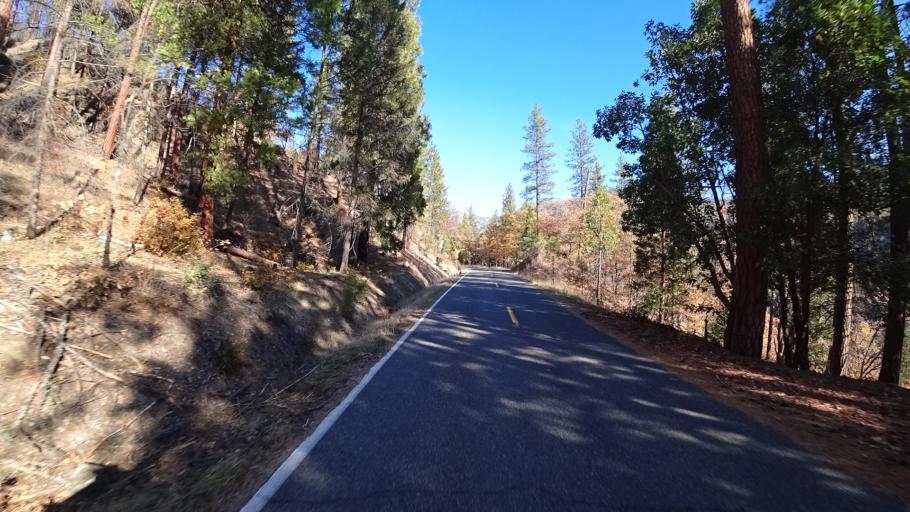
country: US
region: California
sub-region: Siskiyou County
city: Yreka
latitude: 41.8885
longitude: -122.8236
